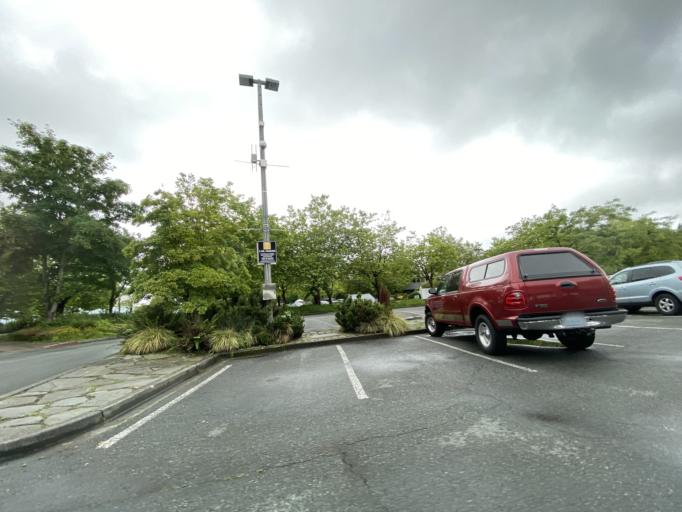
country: US
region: Washington
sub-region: King County
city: Seattle
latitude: 47.6554
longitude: -122.3806
